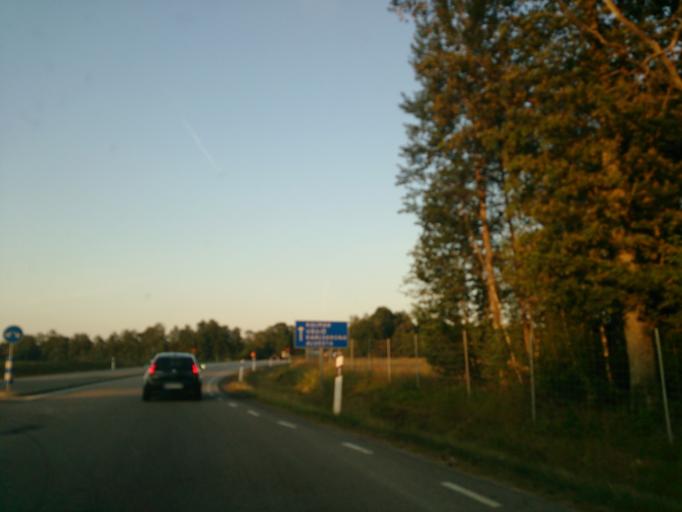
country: SE
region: Kronoberg
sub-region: Alvesta Kommun
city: Alvesta
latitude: 56.9050
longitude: 14.4398
